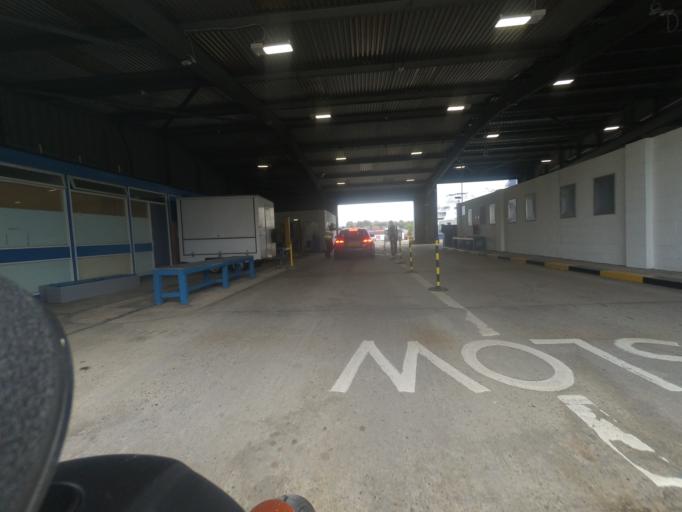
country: GB
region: England
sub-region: South Tyneside
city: South Shields
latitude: 54.9931
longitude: -1.4519
